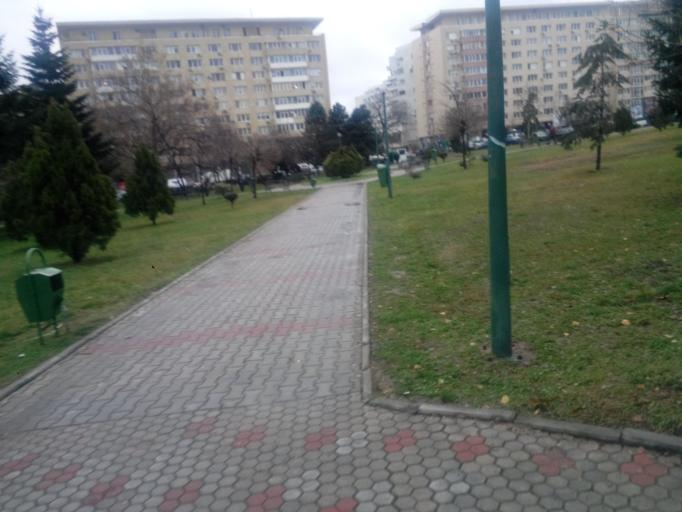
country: RO
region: Bucuresti
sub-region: Municipiul Bucuresti
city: Bucuresti
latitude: 44.4382
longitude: 26.0961
